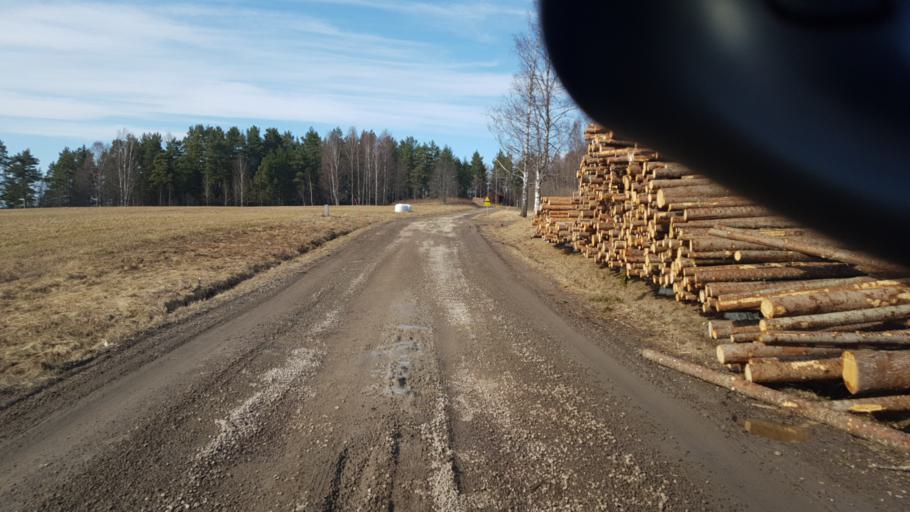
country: SE
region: Vaermland
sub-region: Eda Kommun
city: Amotfors
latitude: 59.7844
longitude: 12.3745
